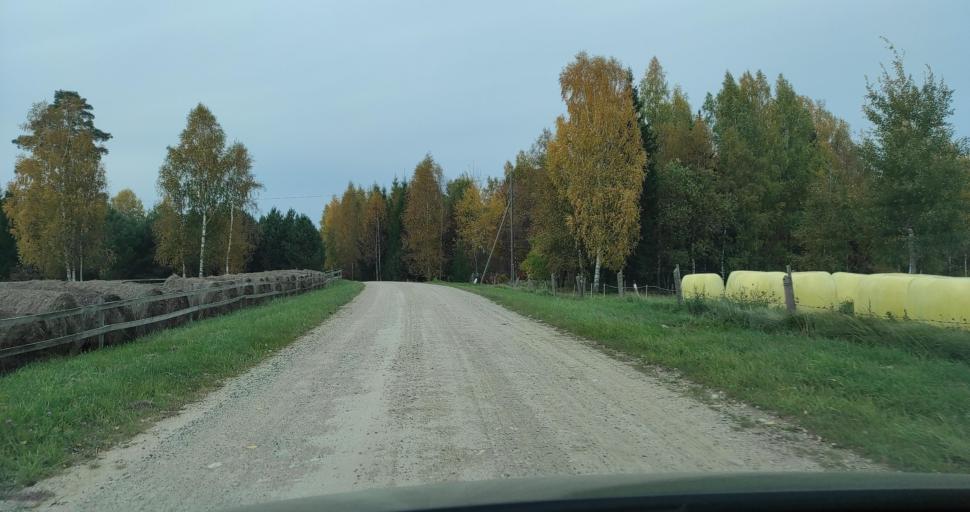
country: LV
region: Kuldigas Rajons
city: Kuldiga
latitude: 57.0262
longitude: 22.1990
